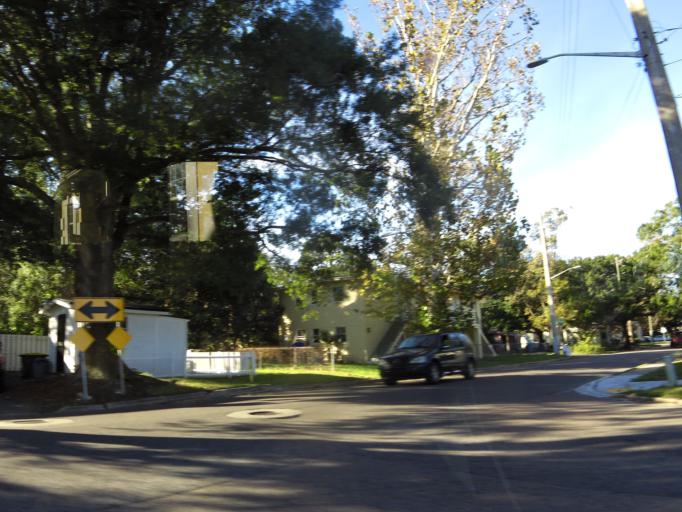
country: US
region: Florida
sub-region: Duval County
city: Jacksonville
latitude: 30.3472
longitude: -81.6799
